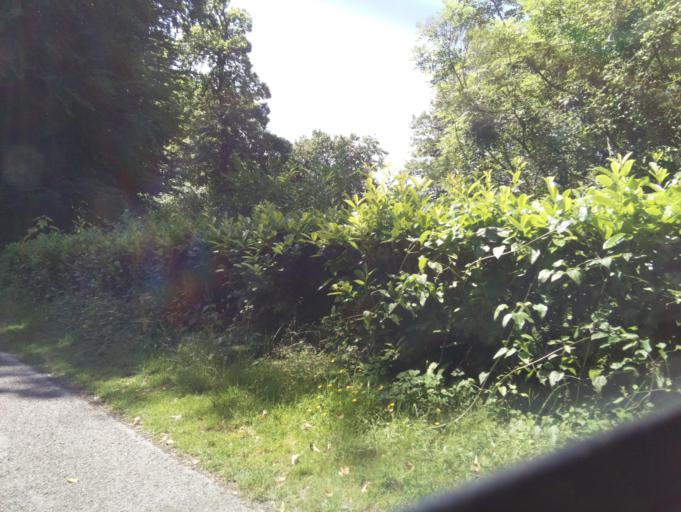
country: GB
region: England
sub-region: Devon
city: Dartmouth
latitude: 50.3825
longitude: -3.5897
